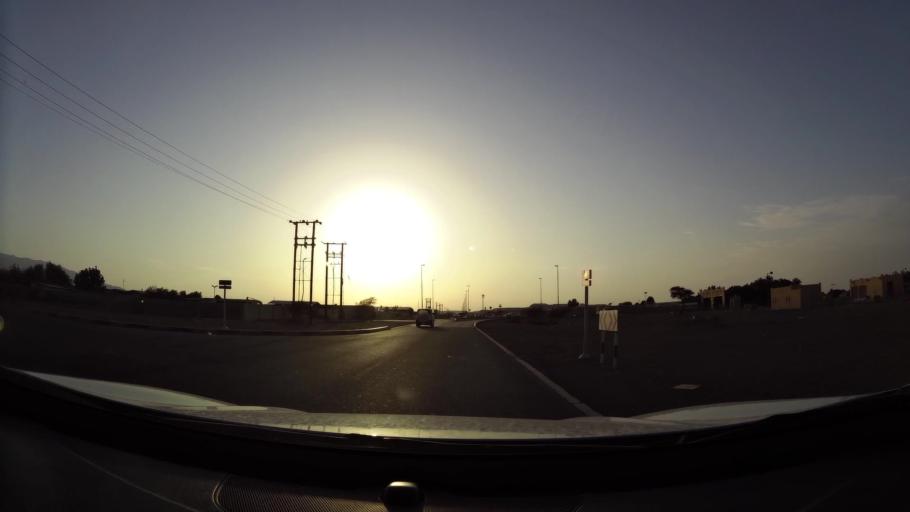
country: AE
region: Abu Dhabi
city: Al Ain
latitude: 24.1591
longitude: 55.8185
